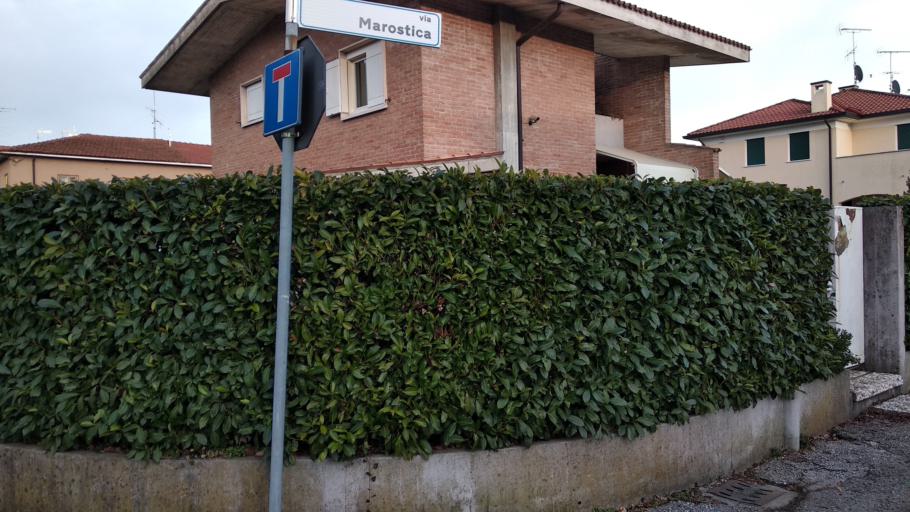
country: IT
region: Veneto
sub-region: Provincia di Vicenza
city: Schio
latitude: 45.7056
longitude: 11.3551
